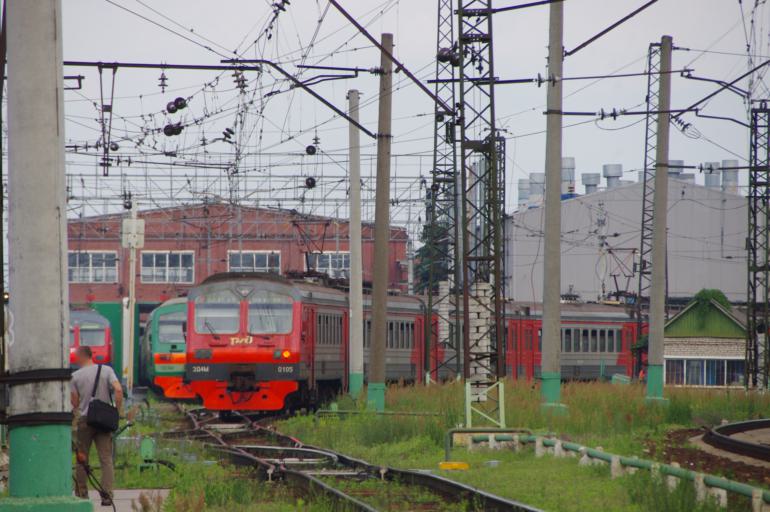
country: RU
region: Moskovskaya
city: Ramenskoye
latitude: 55.5598
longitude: 38.2409
